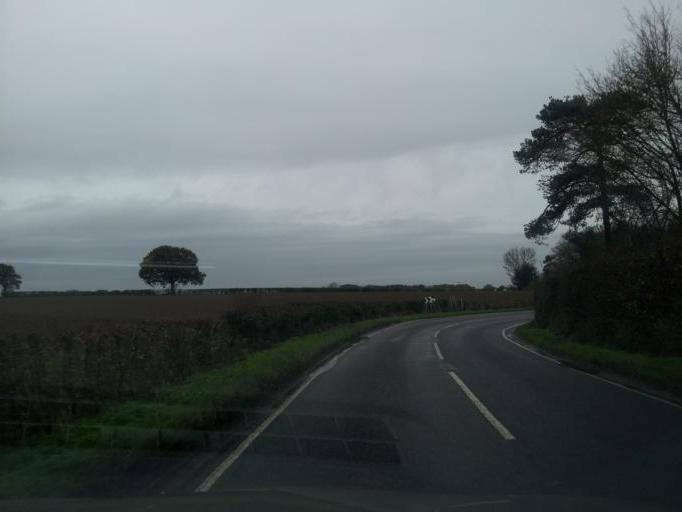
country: GB
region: England
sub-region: Essex
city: West Bergholt
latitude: 51.9366
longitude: 0.8285
